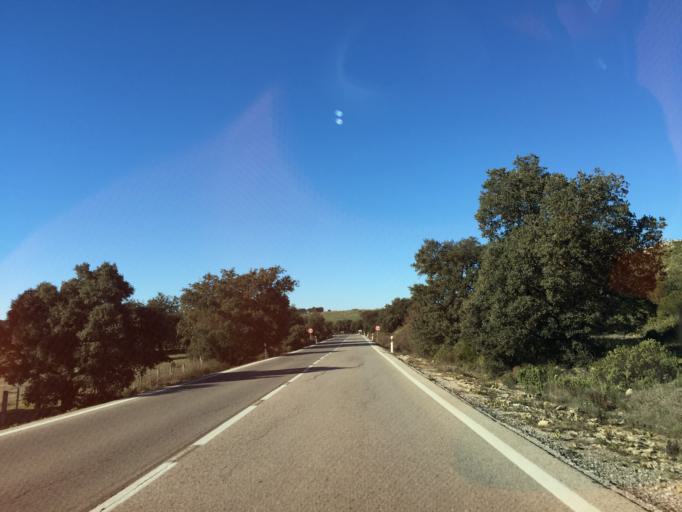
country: ES
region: Andalusia
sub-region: Provincia de Malaga
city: Cuevas del Becerro
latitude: 36.8394
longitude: -5.0640
